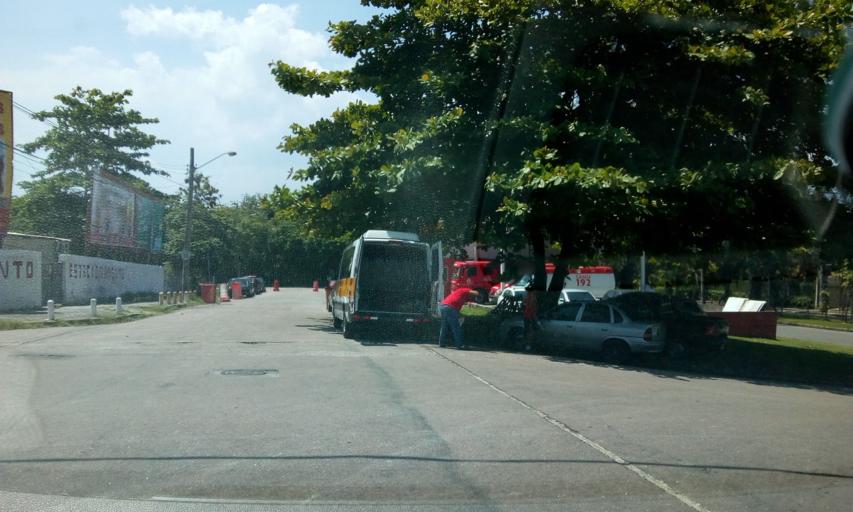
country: BR
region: Rio de Janeiro
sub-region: Nilopolis
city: Nilopolis
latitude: -23.0238
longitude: -43.4579
